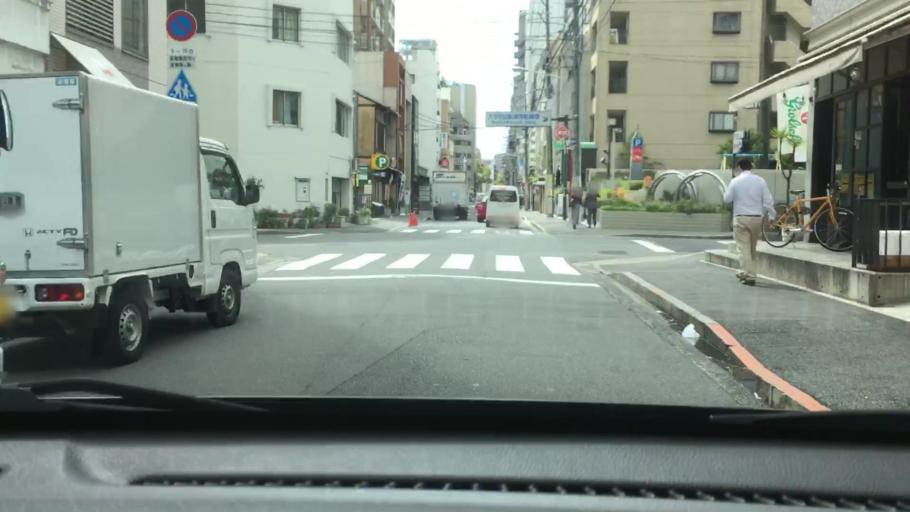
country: JP
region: Hiroshima
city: Hiroshima-shi
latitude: 34.3930
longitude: 132.4555
